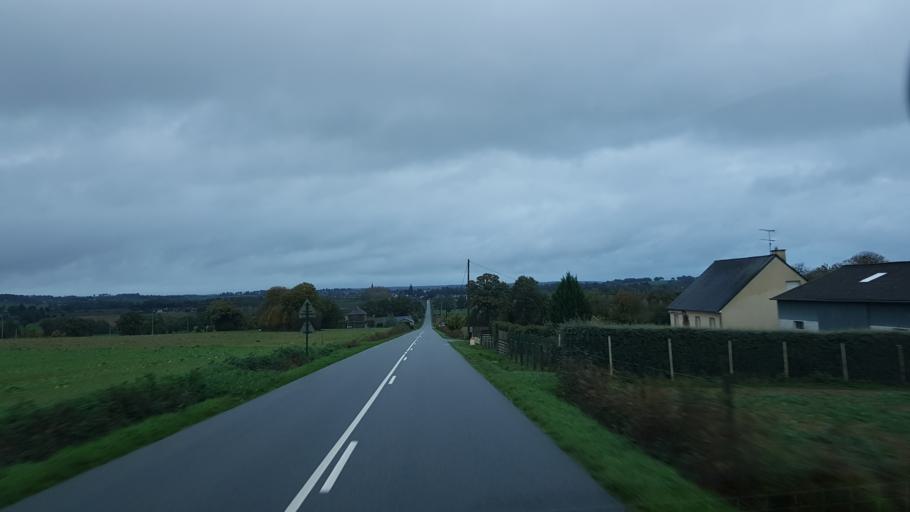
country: FR
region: Brittany
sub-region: Departement d'Ille-et-Vilaine
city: Balaze
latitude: 48.1627
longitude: -1.1340
